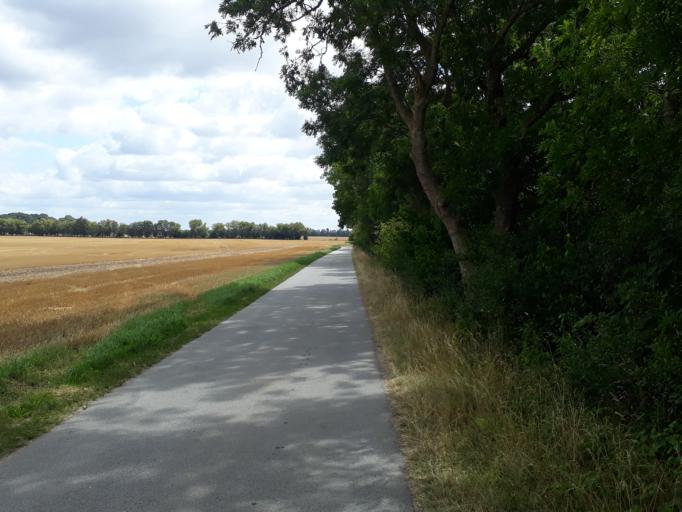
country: DE
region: Mecklenburg-Vorpommern
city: Marlow
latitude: 54.2174
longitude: 12.5626
